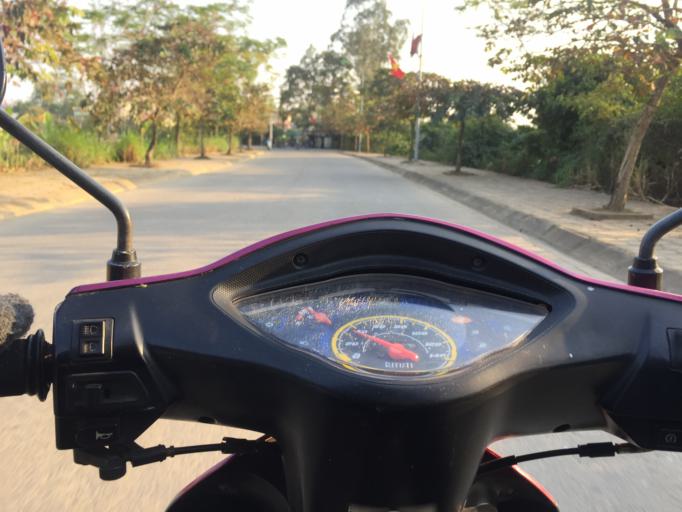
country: VN
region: Ha Noi
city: Chuc Son
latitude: 20.9222
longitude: 105.7100
